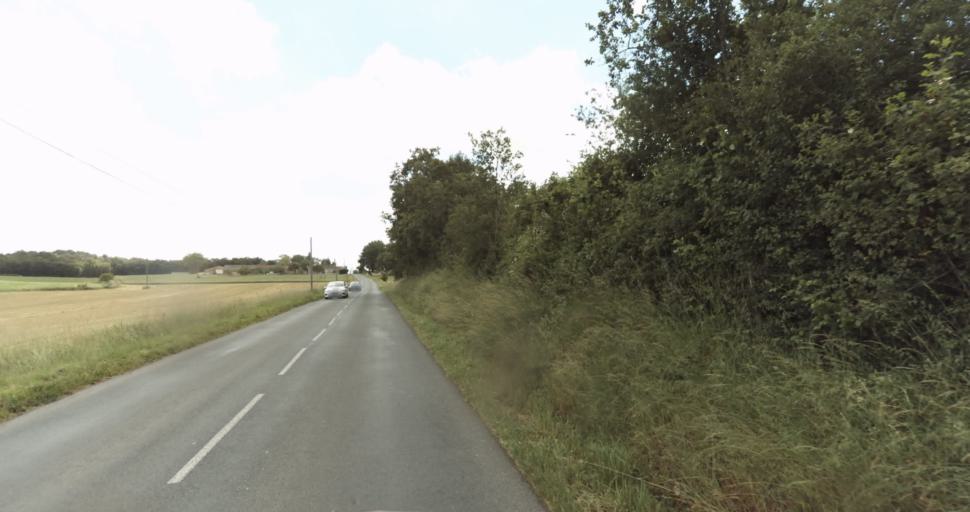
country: FR
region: Aquitaine
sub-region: Departement de la Dordogne
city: Beaumont-du-Perigord
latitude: 44.7358
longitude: 0.7527
